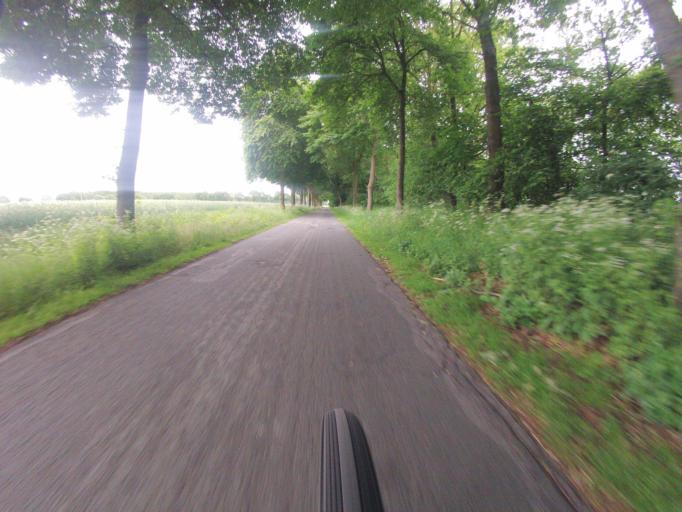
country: DE
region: North Rhine-Westphalia
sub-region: Regierungsbezirk Munster
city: Saerbeck
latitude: 52.1770
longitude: 7.6057
